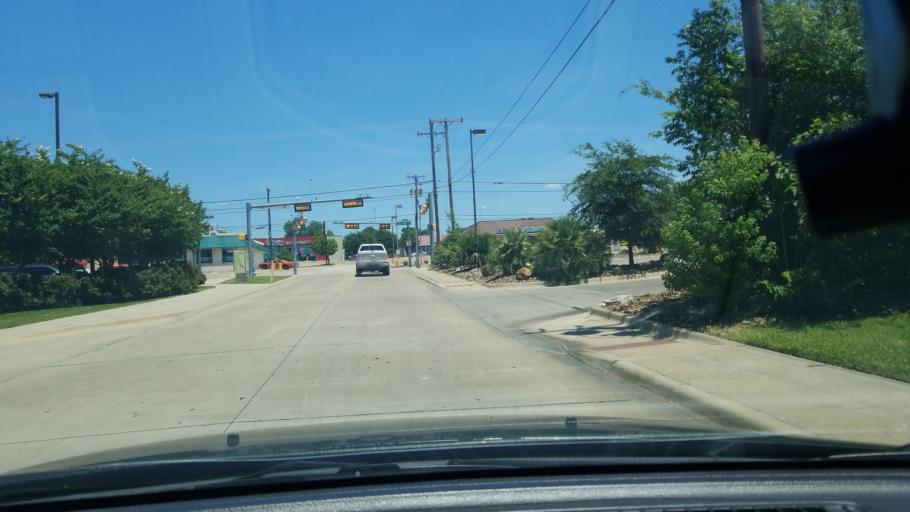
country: US
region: Texas
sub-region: Dallas County
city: Mesquite
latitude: 32.7728
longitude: -96.6000
